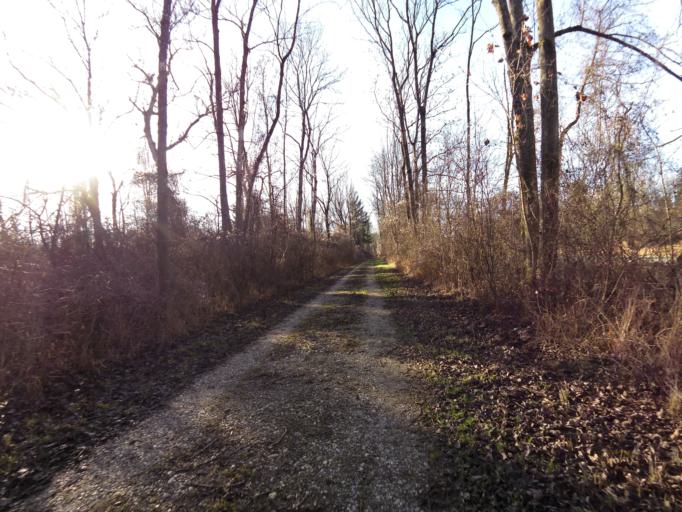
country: DE
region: Bavaria
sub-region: Lower Bavaria
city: Bruckberg
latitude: 48.4988
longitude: 12.0156
